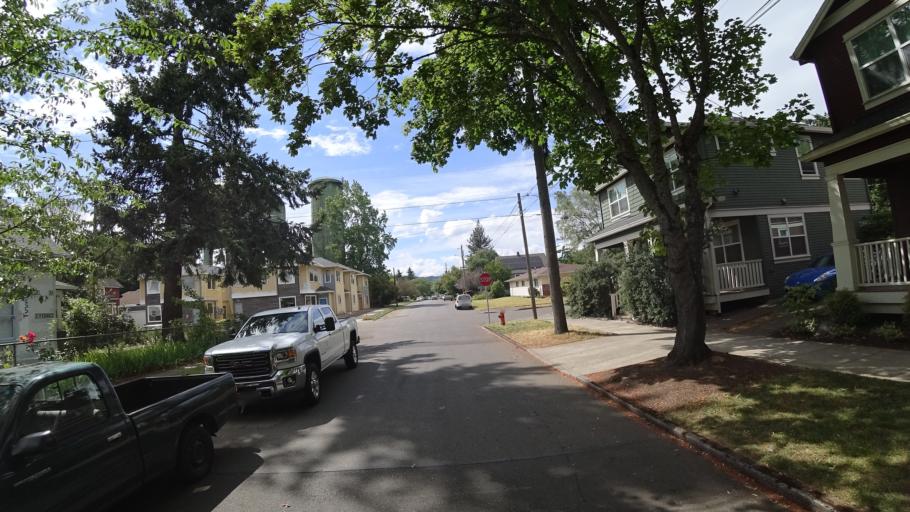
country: US
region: Oregon
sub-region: Washington County
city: West Haven
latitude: 45.5863
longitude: -122.7502
